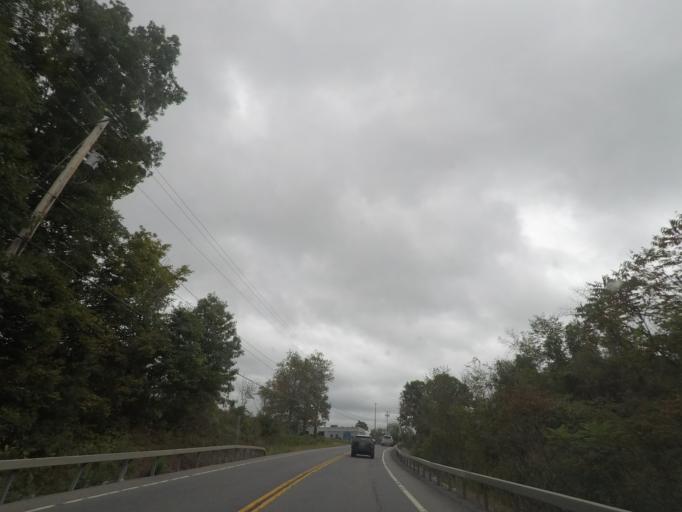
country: US
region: New York
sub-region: Saratoga County
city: Mechanicville
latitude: 42.9187
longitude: -73.7141
